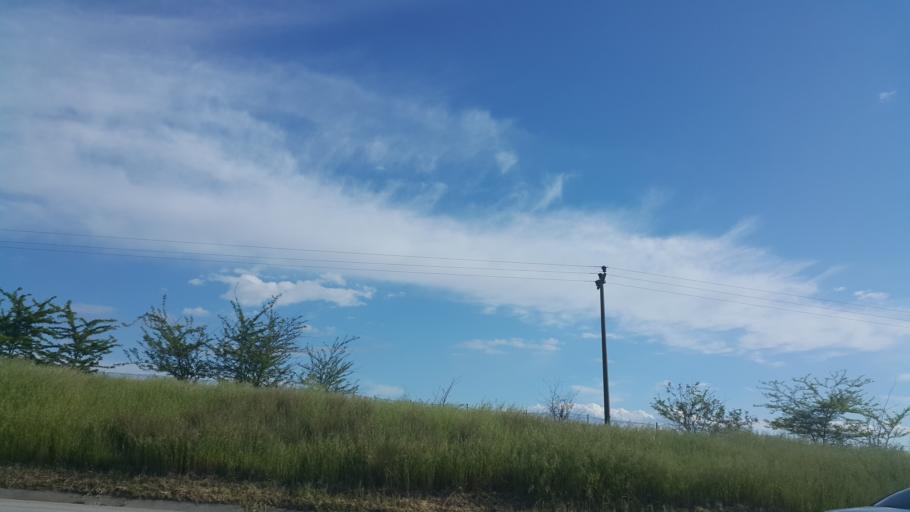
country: TR
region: Adana
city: Yuregir
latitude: 37.0278
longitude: 35.4233
